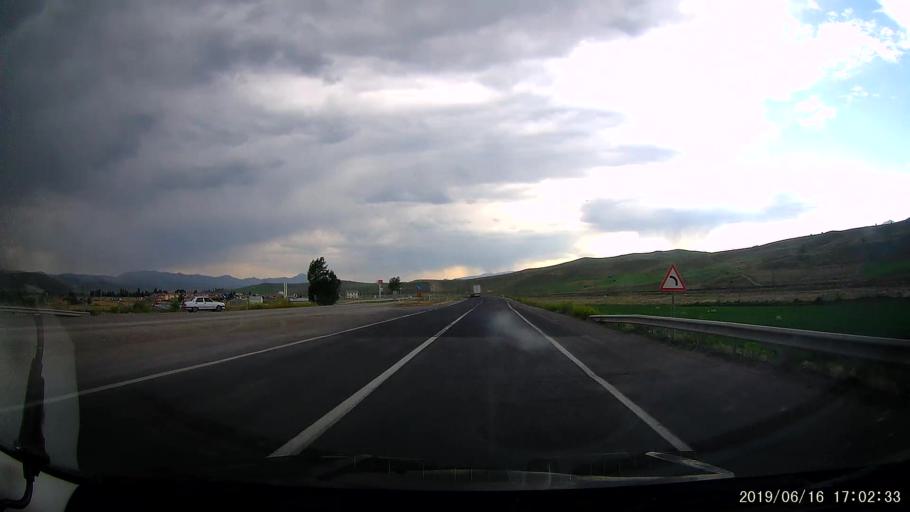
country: TR
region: Erzurum
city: Askale
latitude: 39.9403
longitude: 40.7518
